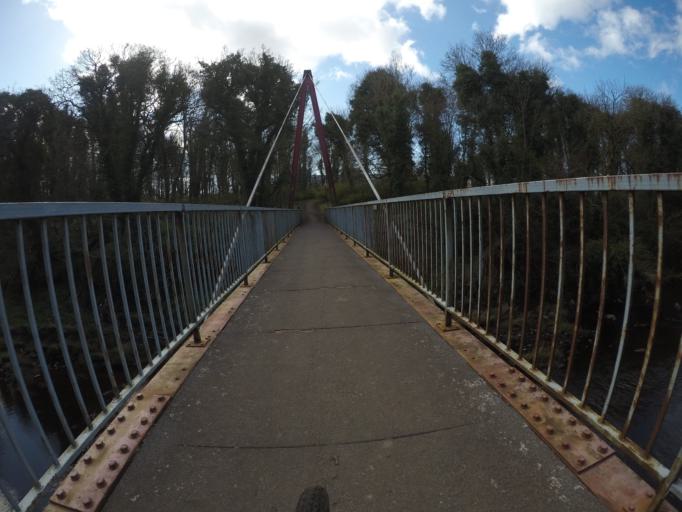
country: GB
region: Scotland
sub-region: North Ayrshire
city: Dreghorn
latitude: 55.5973
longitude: -4.6263
